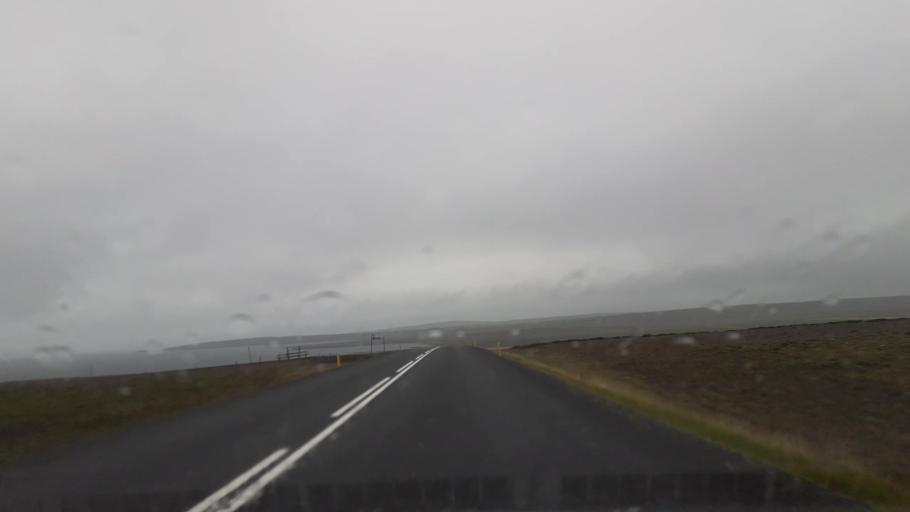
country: IS
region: Northeast
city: Husavik
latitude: 66.2311
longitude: -15.7249
